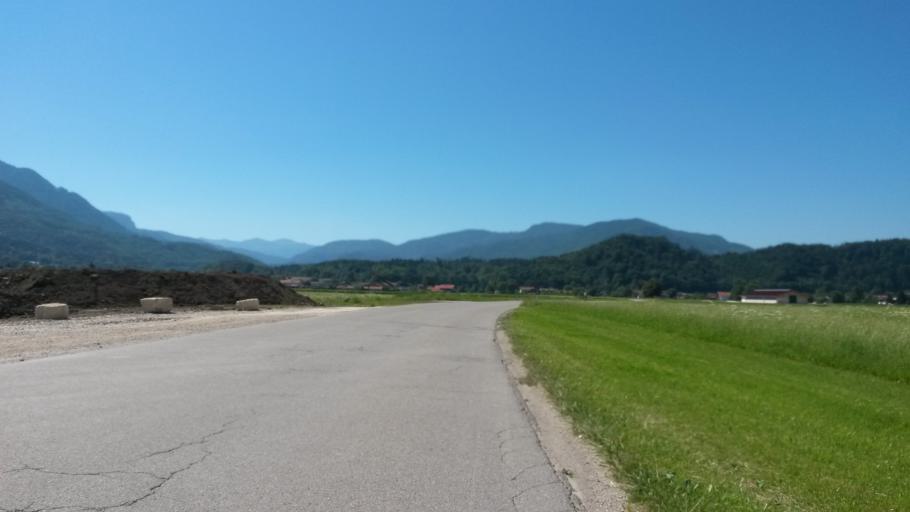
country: DE
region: Bavaria
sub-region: Upper Bavaria
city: Grassau
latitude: 47.7711
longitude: 12.4554
